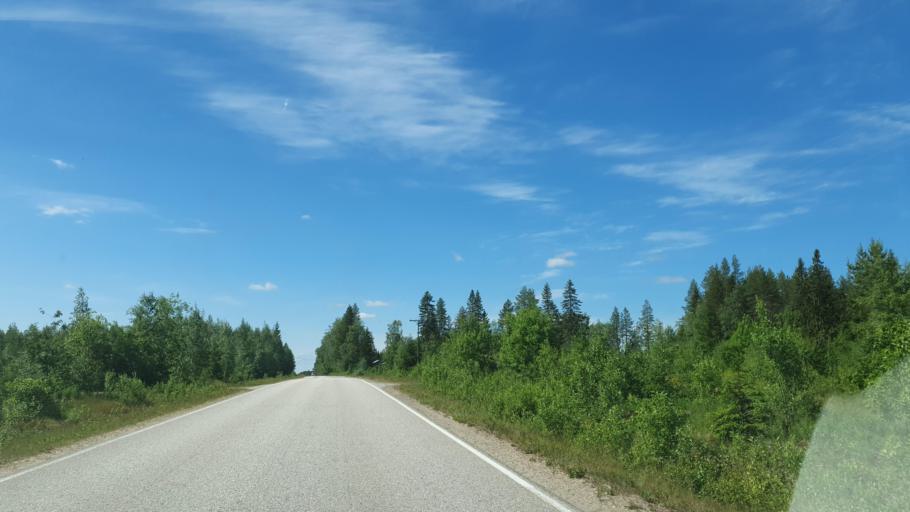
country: FI
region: Kainuu
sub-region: Kehys-Kainuu
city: Suomussalmi
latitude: 64.5881
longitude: 29.0684
